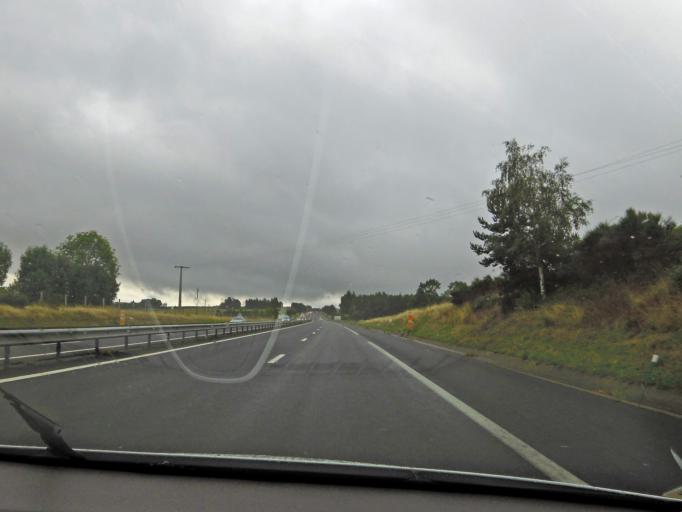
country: FR
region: Auvergne
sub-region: Departement du Cantal
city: Saint-Flour
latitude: 44.9501
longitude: 3.1971
